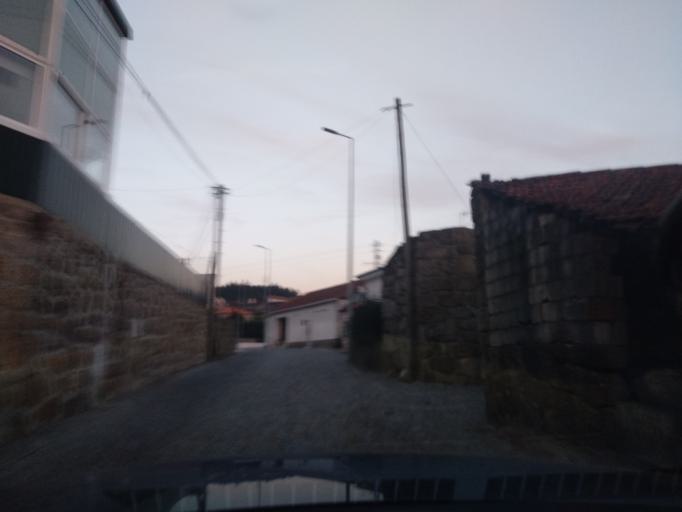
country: PT
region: Porto
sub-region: Paredes
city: Lordelo
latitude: 41.2348
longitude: -8.4069
